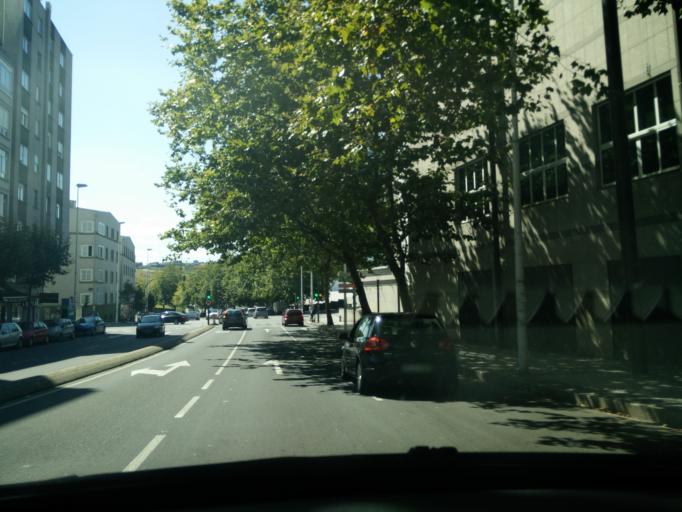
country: ES
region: Galicia
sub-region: Provincia da Coruna
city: A Coruna
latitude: 43.3733
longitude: -8.4250
